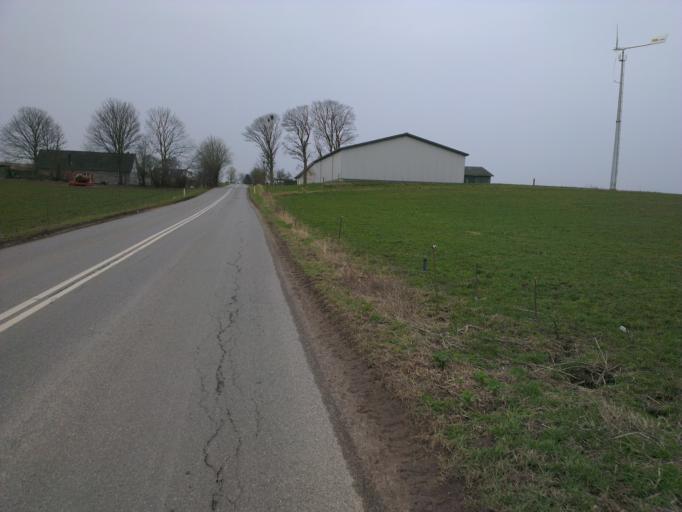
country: DK
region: Capital Region
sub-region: Frederikssund Kommune
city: Skibby
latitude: 55.7439
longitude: 11.9272
